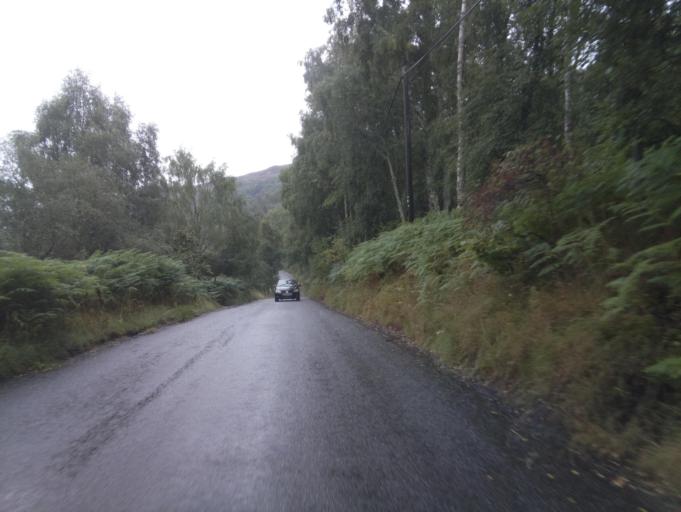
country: GB
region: Scotland
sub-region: Aberdeenshire
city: Ballater
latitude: 57.0781
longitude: -3.0875
